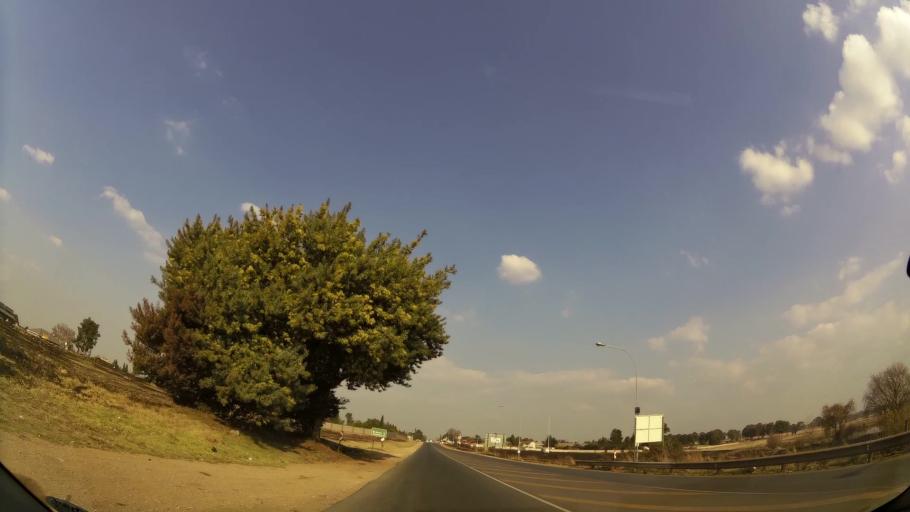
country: ZA
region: Gauteng
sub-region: Ekurhuleni Metropolitan Municipality
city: Tembisa
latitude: -26.0805
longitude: 28.2863
